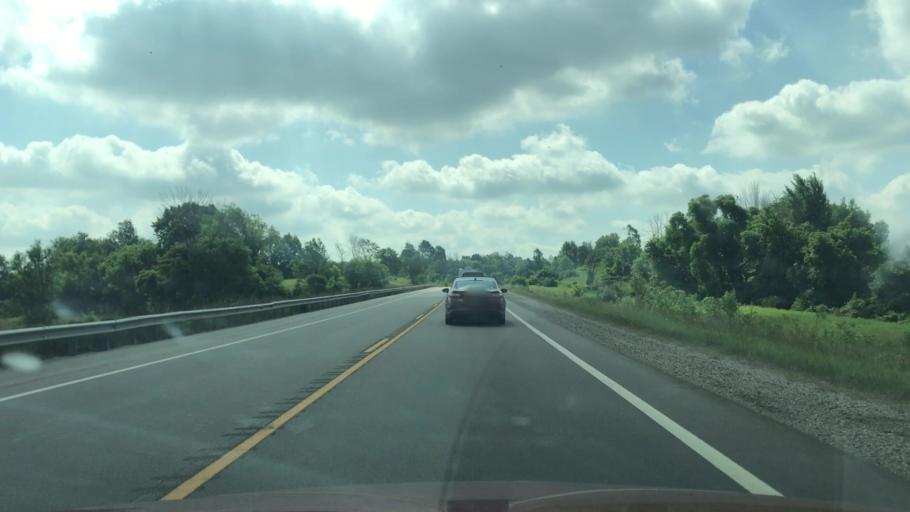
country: US
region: Michigan
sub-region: Kent County
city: Kent City
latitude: 43.2008
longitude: -85.7293
